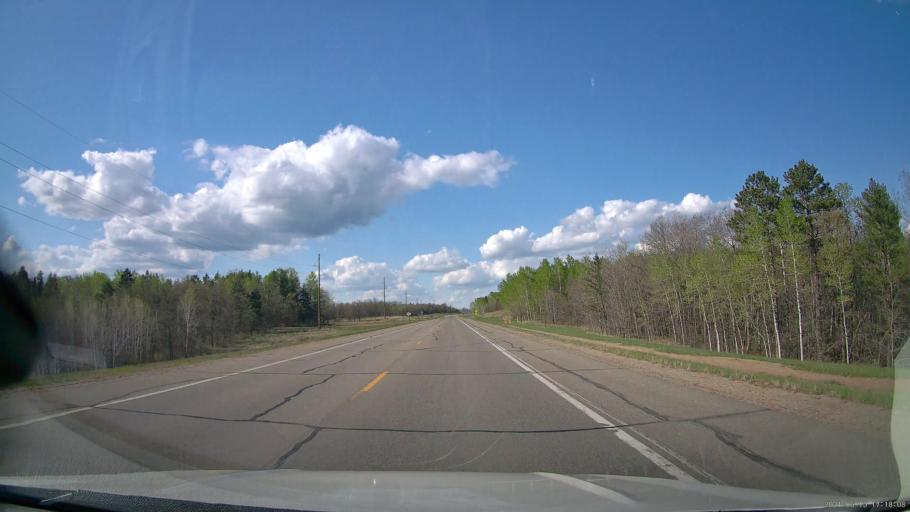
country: US
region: Minnesota
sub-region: Hubbard County
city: Park Rapids
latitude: 46.9564
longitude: -95.0185
